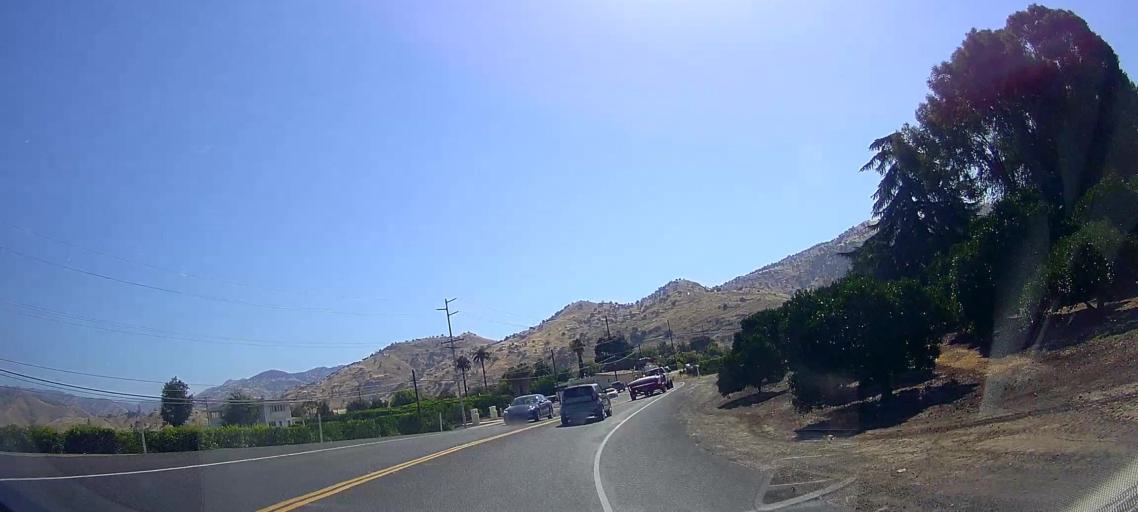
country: US
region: California
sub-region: Tulare County
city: Woodlake
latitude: 36.3861
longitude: -119.0240
